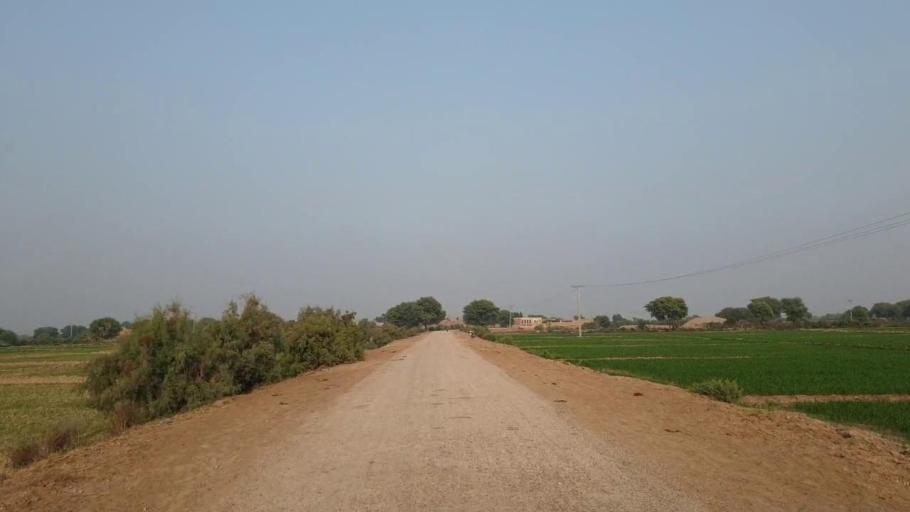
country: PK
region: Sindh
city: Bhan
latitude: 26.5023
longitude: 67.7557
